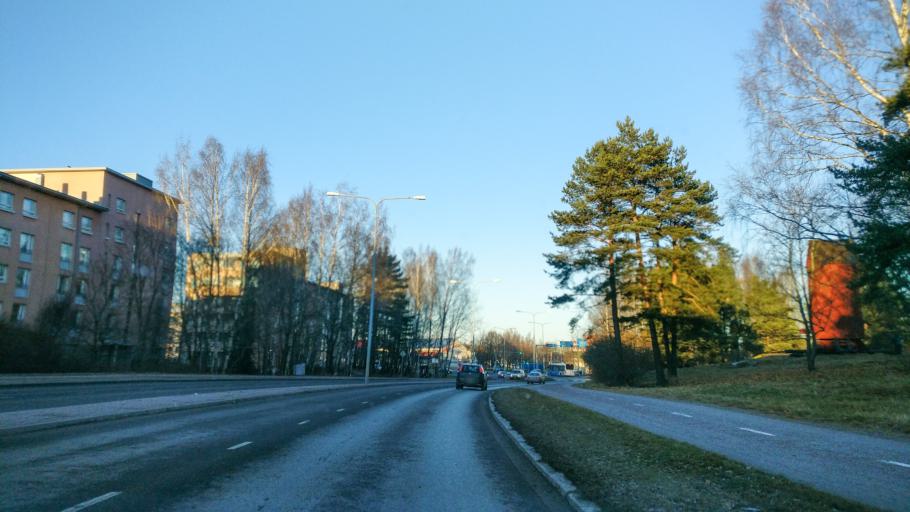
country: FI
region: Uusimaa
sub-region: Helsinki
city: Vantaa
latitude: 60.1904
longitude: 25.0401
